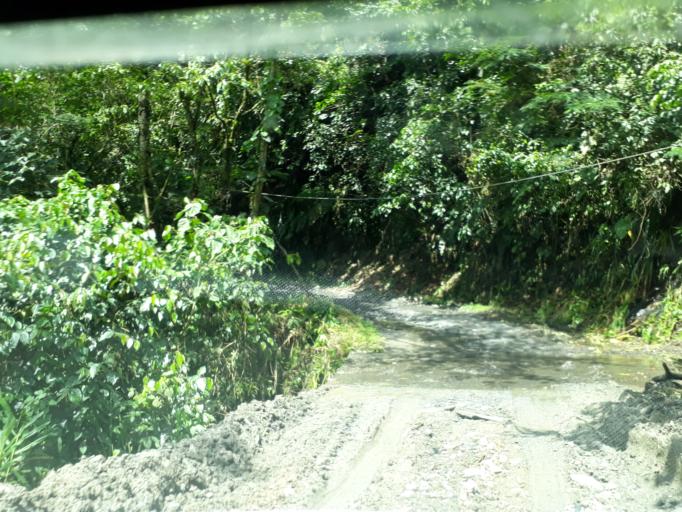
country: CO
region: Cundinamarca
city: Topaipi
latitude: 5.3132
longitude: -74.2120
